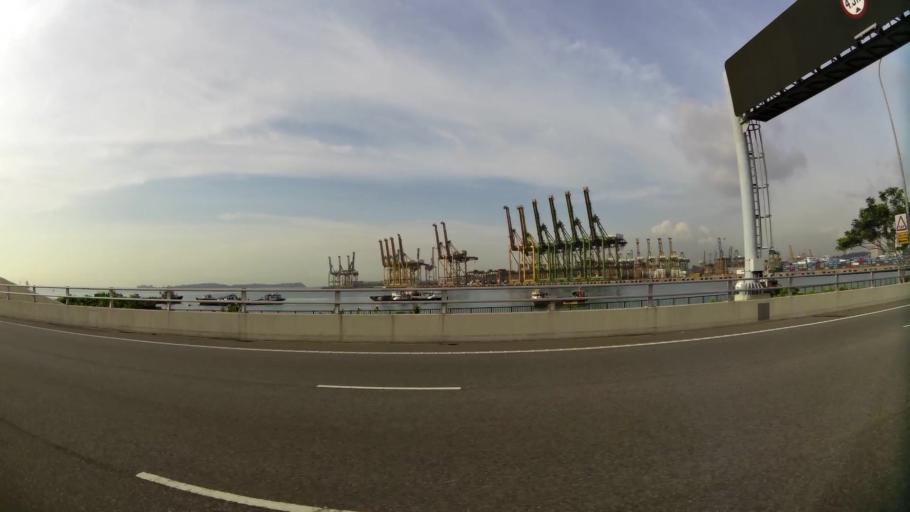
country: SG
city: Singapore
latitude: 1.2718
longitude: 103.8547
